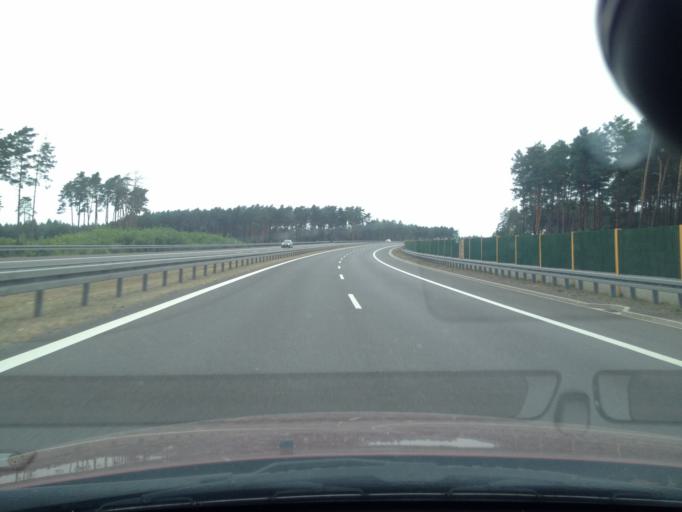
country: PL
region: Lubusz
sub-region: Powiat miedzyrzecki
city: Skwierzyna
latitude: 52.5578
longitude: 15.4793
